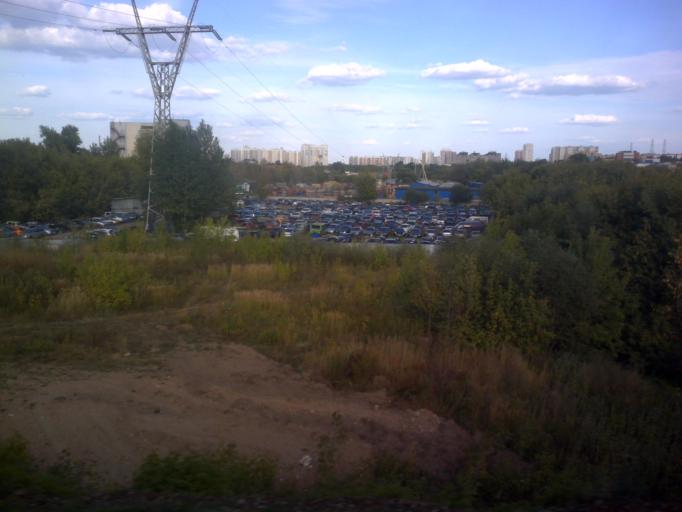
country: RU
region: Moscow
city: Nagornyy
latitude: 55.6405
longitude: 37.6250
